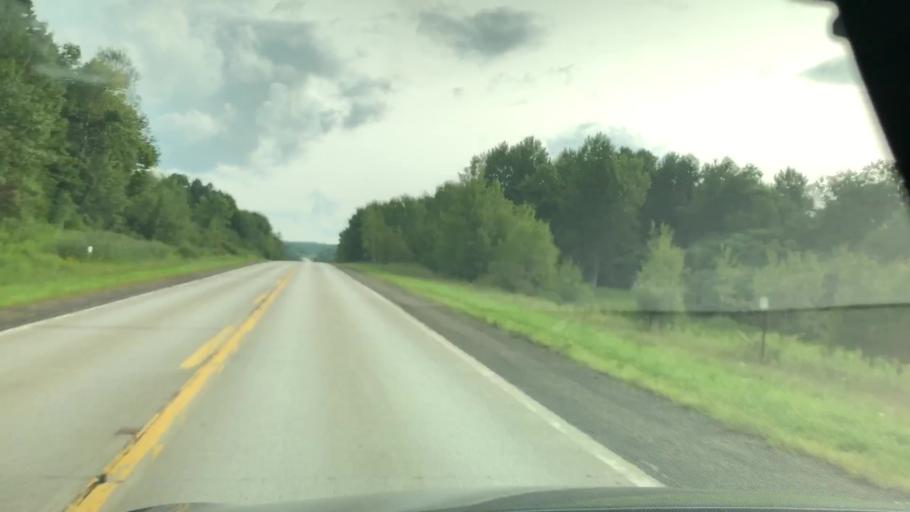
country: US
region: Pennsylvania
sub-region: Erie County
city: Union City
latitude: 41.9757
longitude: -79.8428
